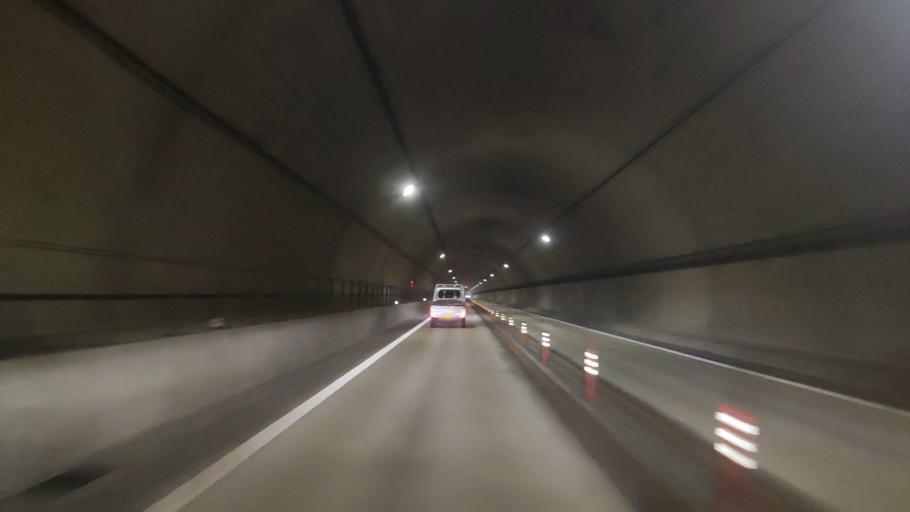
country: JP
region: Wakayama
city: Tanabe
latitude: 33.6239
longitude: 135.4181
